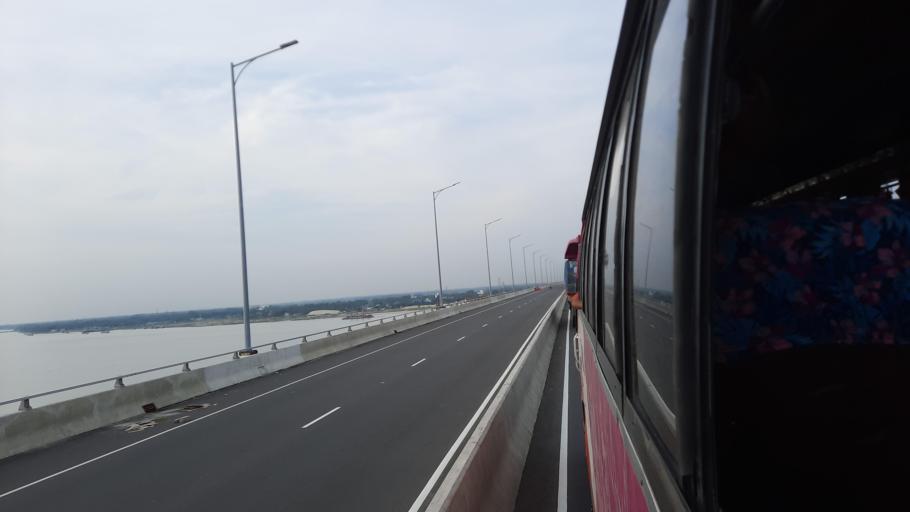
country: BD
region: Dhaka
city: Char Bhadrasan
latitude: 23.4589
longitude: 90.2624
